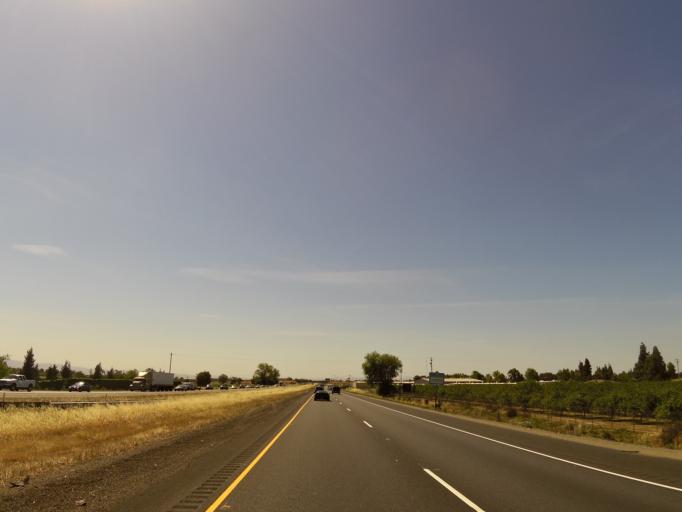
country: US
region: California
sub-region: San Joaquin County
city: Manteca
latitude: 37.7835
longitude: -121.2044
